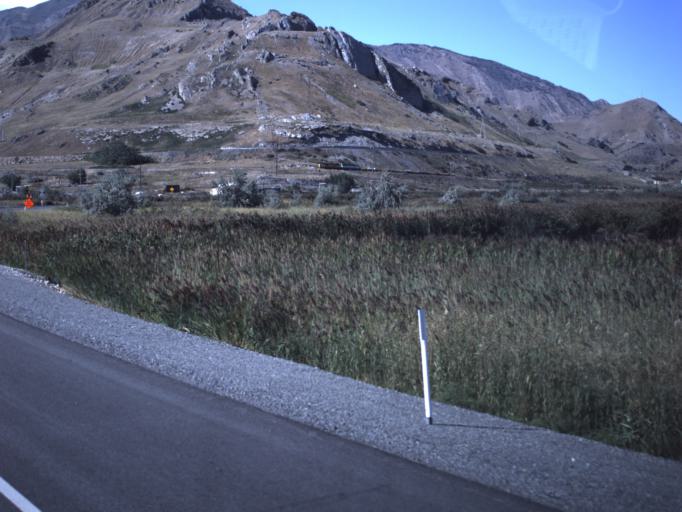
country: US
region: Utah
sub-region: Salt Lake County
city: Magna
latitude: 40.7319
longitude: -112.1687
